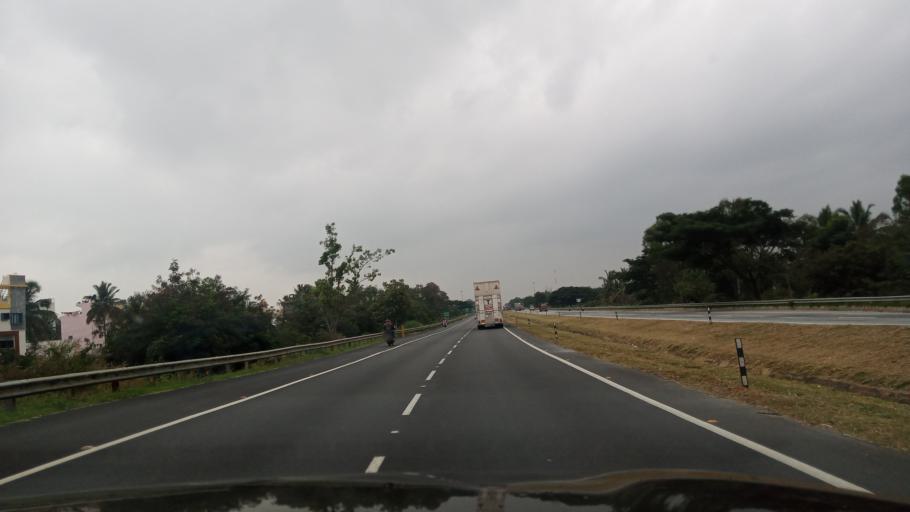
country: IN
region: Karnataka
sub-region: Bangalore Urban
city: Bangalore
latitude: 12.9975
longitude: 77.4739
